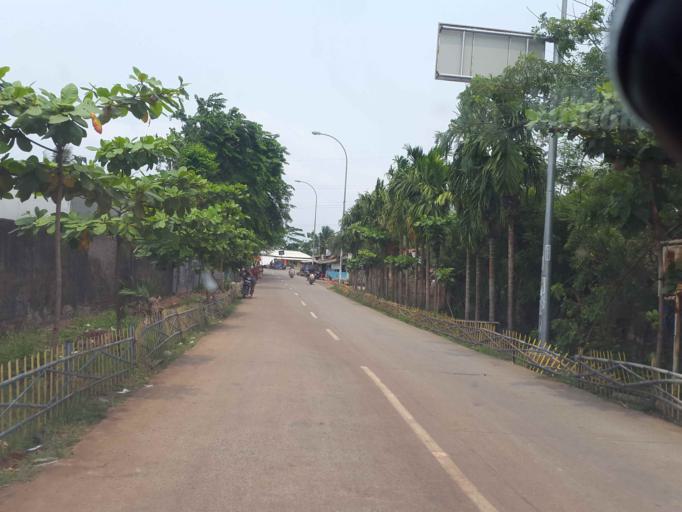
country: ID
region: West Java
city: Cikarang
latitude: -6.2701
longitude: 107.2661
